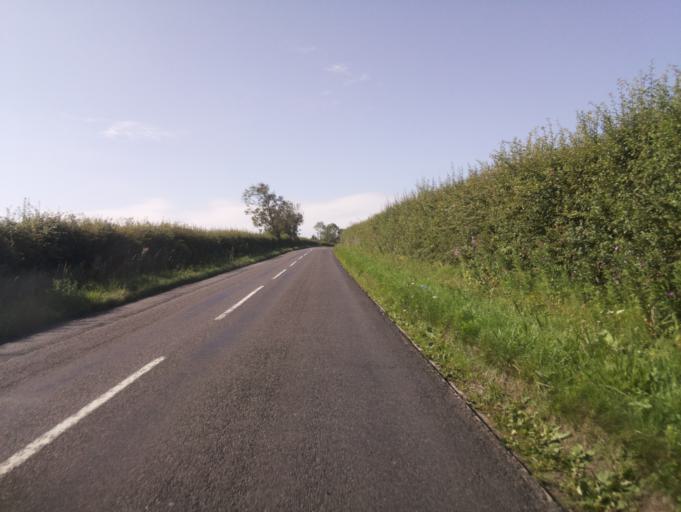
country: GB
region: England
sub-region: Oxfordshire
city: Ducklington
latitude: 51.7601
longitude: -1.4869
